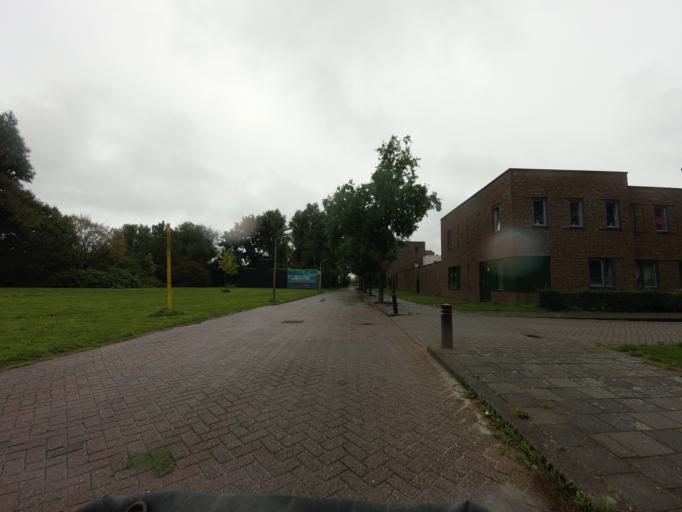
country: NL
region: Friesland
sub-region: Gemeente Leeuwarden
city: Bilgaard
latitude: 53.2169
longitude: 5.8056
